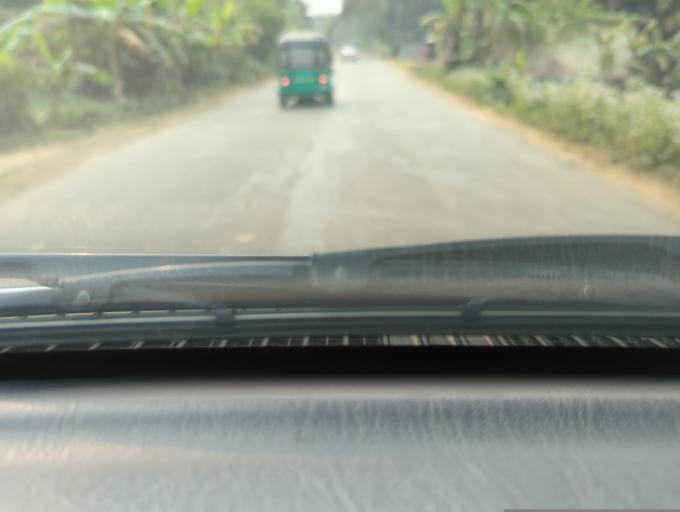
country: BD
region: Sylhet
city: Maulavi Bazar
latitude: 24.5259
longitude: 91.7329
